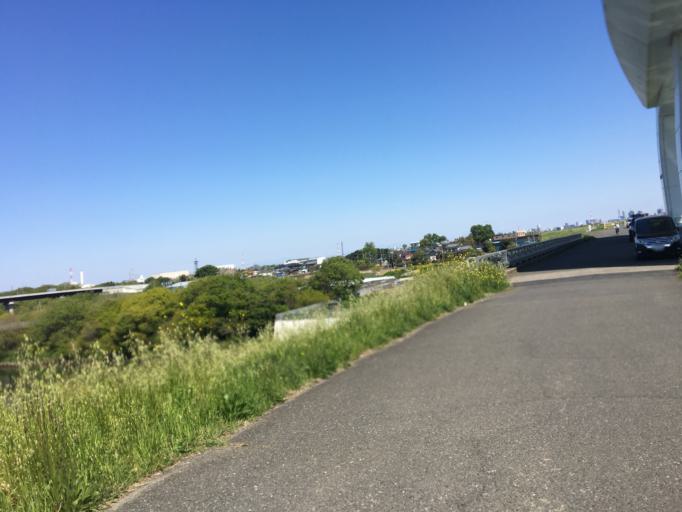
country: JP
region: Saitama
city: Asaka
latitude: 35.8111
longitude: 139.6190
